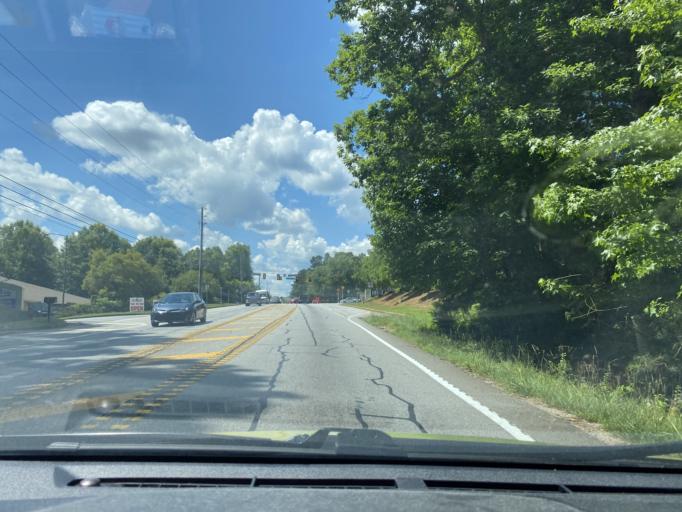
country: US
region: Georgia
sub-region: Fayette County
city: Peachtree City
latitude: 33.4125
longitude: -84.6827
